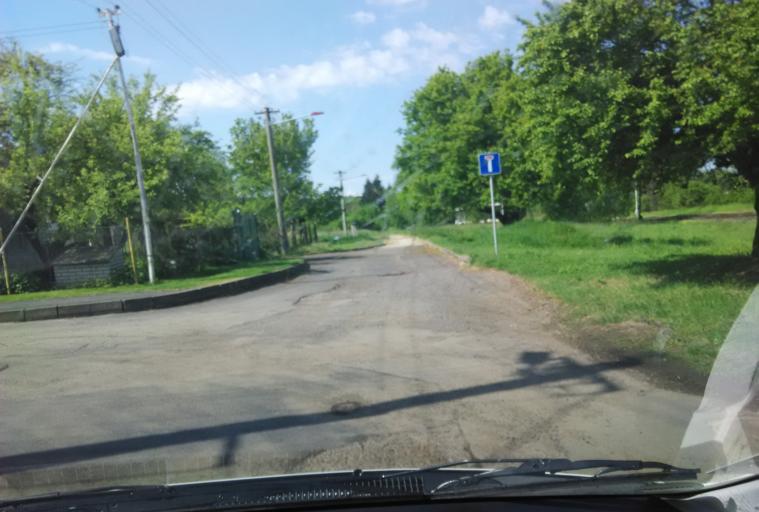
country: SK
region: Banskobystricky
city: Dudince
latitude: 48.1678
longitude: 18.8907
